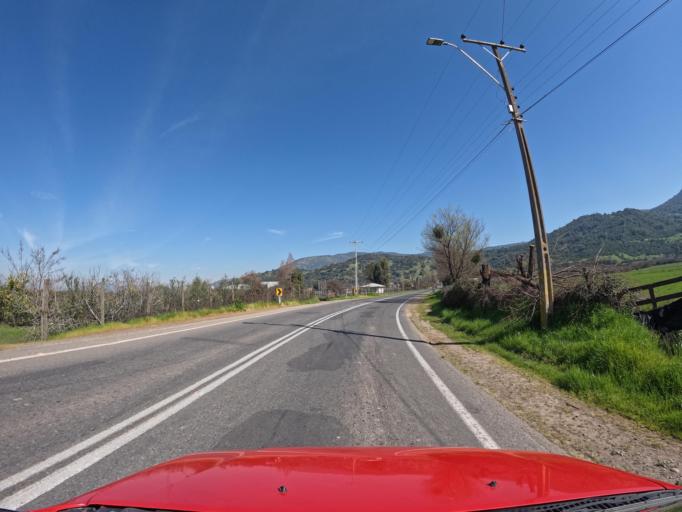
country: CL
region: Maule
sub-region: Provincia de Curico
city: Rauco
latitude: -34.9817
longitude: -71.4143
